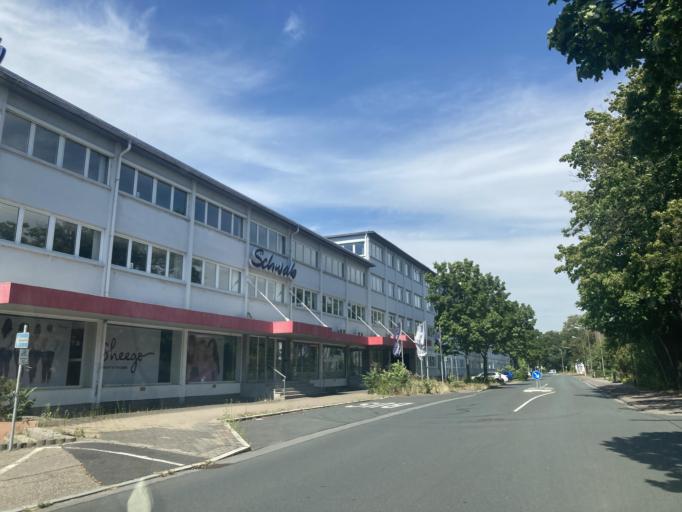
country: DE
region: Hesse
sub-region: Regierungsbezirk Darmstadt
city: Hanau am Main
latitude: 50.1217
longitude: 8.9216
